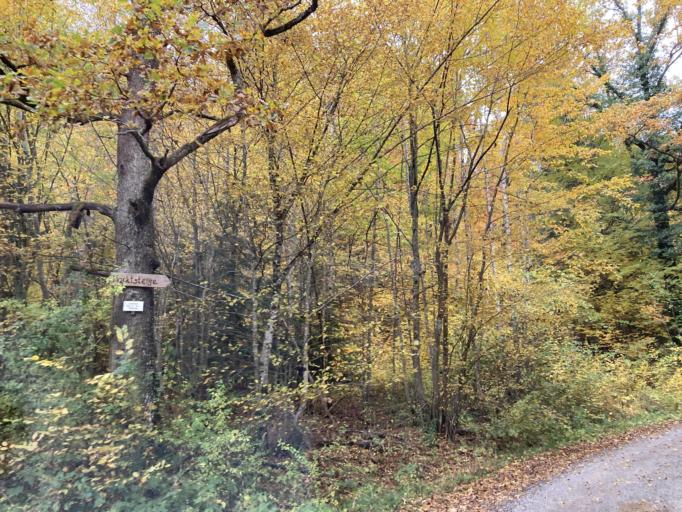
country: DE
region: Baden-Wuerttemberg
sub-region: Tuebingen Region
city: Dusslingen
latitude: 48.4677
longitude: 8.9989
